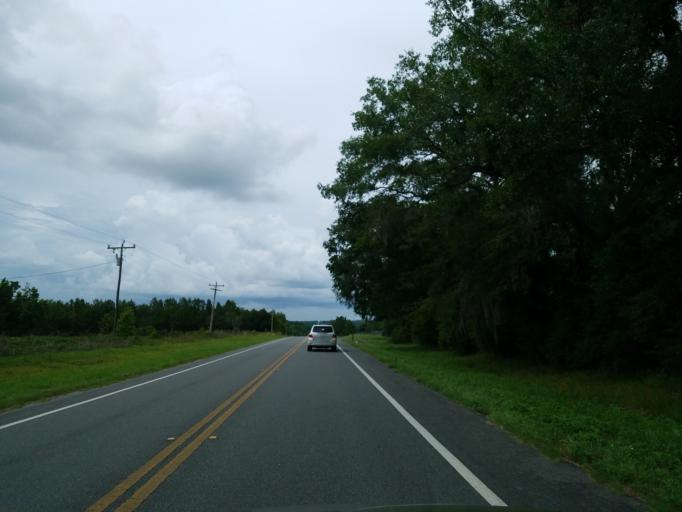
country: US
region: Florida
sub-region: Alachua County
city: High Springs
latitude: 29.9234
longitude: -82.5056
